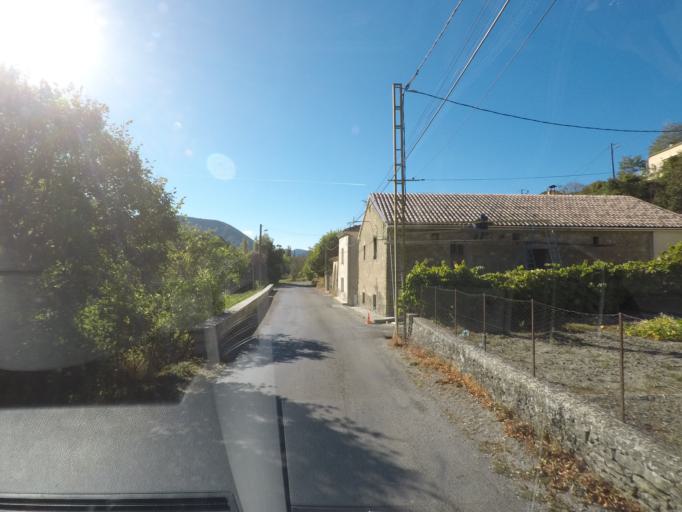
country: FR
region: Provence-Alpes-Cote d'Azur
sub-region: Departement des Hautes-Alpes
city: Serres
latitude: 44.4677
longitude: 5.5139
